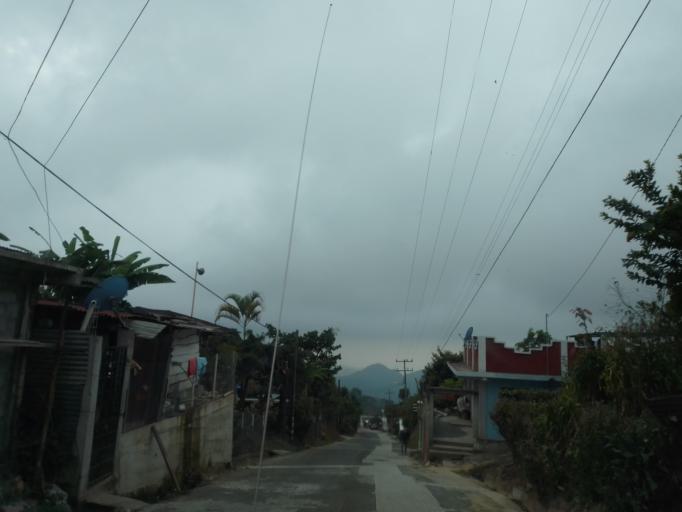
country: MX
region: Chiapas
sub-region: Union Juarez
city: Santo Domingo
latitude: 15.0778
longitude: -92.0812
